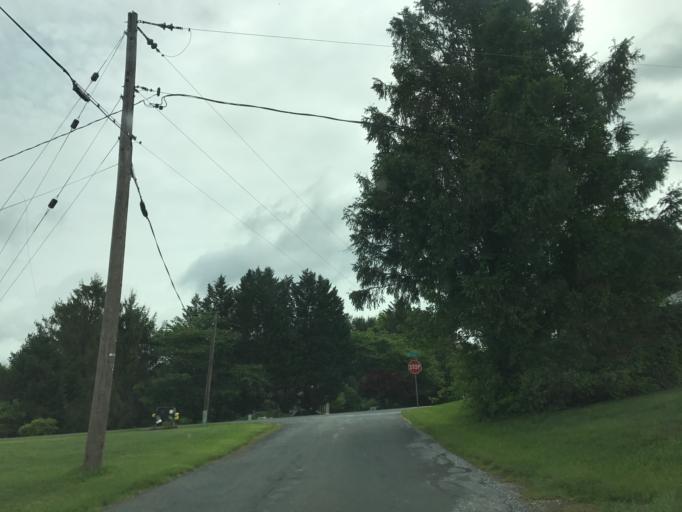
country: US
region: Maryland
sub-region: Carroll County
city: Hampstead
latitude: 39.5470
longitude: -76.8793
